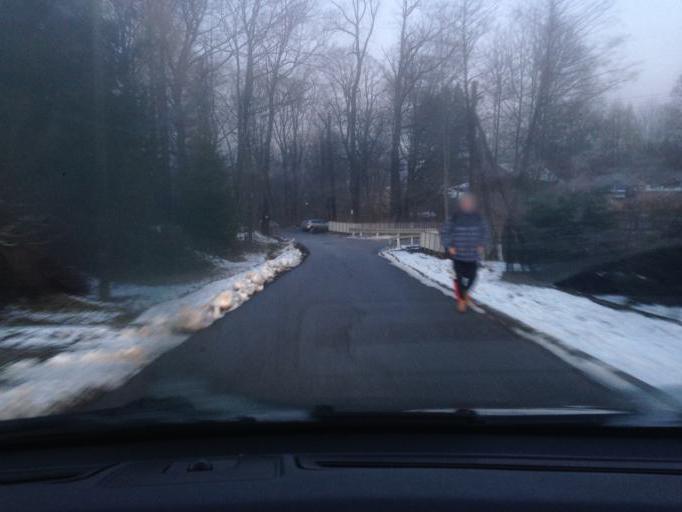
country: PL
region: Silesian Voivodeship
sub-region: Powiat bielski
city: Bystra
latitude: 49.7831
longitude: 19.0329
